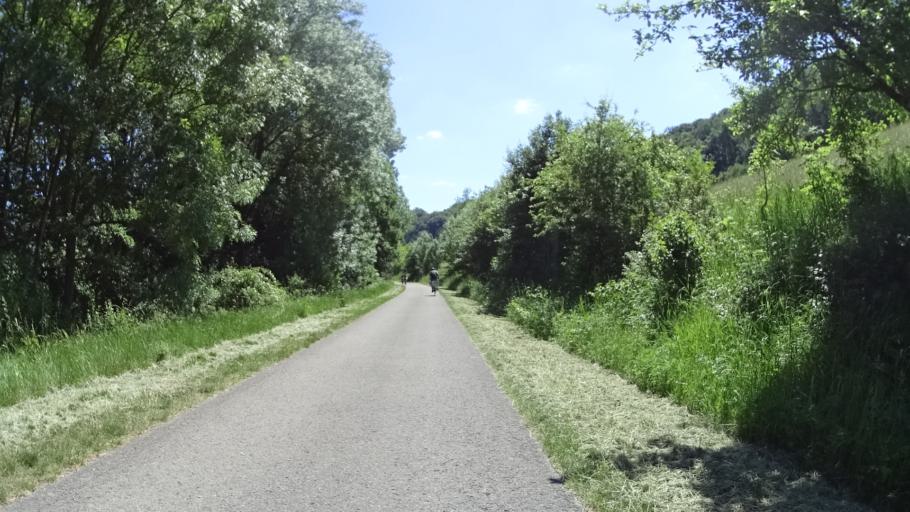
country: DE
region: Bavaria
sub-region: Regierungsbezirk Mittelfranken
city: Adelshofen
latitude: 49.4432
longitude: 10.1244
